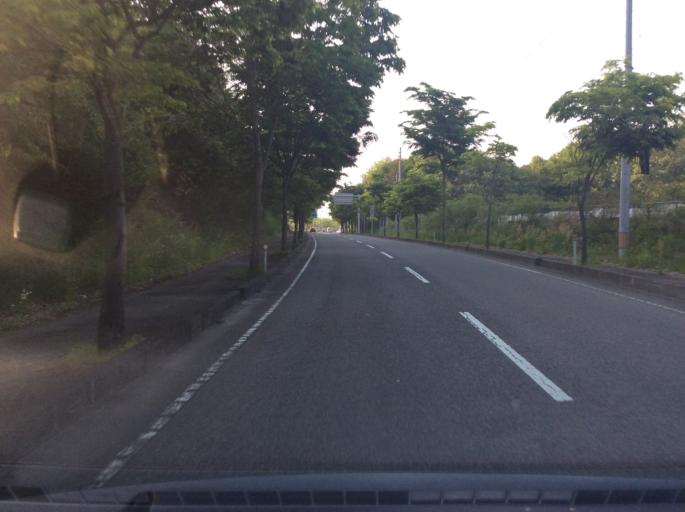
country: JP
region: Fukushima
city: Ishikawa
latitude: 37.2220
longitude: 140.4363
